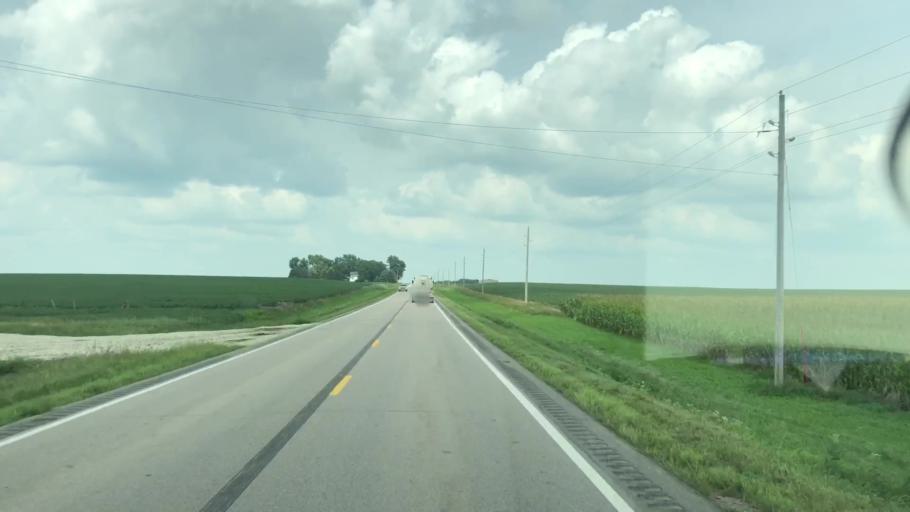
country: US
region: Iowa
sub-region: Plymouth County
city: Remsen
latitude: 42.7854
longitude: -95.9578
